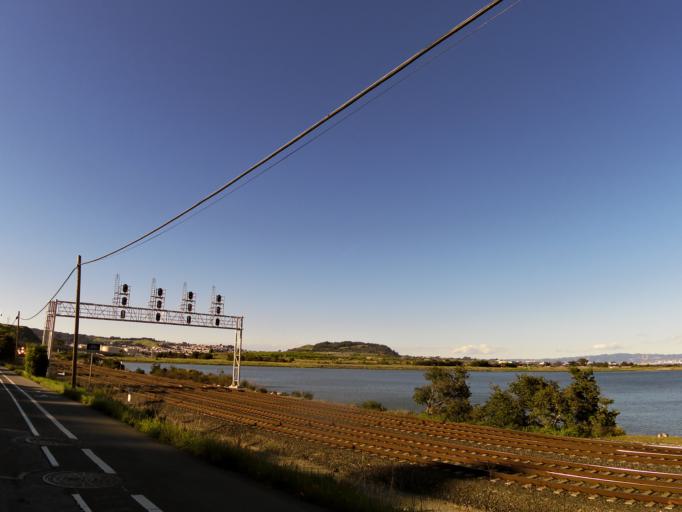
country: US
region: California
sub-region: San Mateo County
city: Brisbane
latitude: 37.6832
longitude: -122.3957
